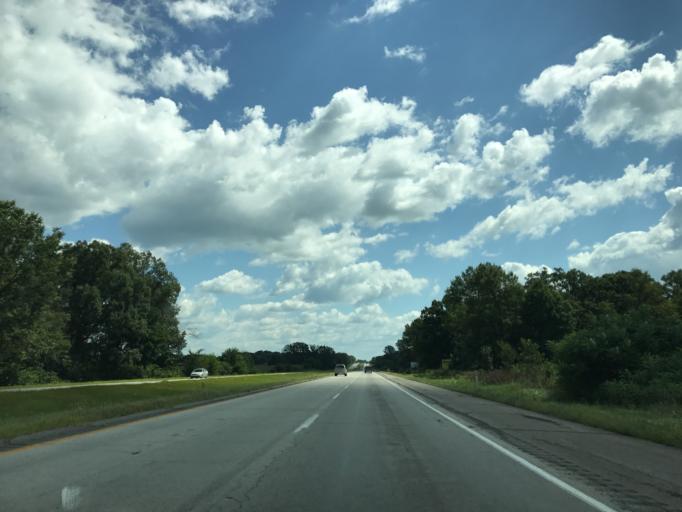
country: US
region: Indiana
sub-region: Starke County
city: Koontz Lake
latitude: 41.3645
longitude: -86.4125
